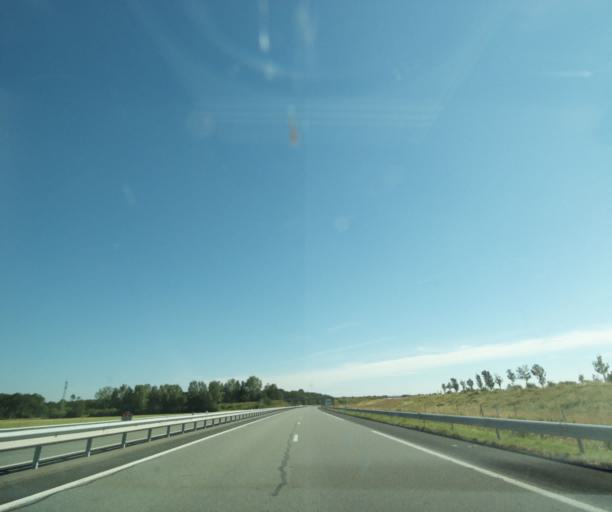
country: FR
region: Lorraine
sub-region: Departement des Vosges
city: Lamarche
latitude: 48.1291
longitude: 5.6685
